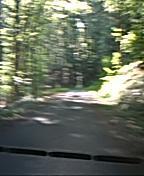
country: FR
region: Rhone-Alpes
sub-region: Departement de la Loire
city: La Pacaudiere
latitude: 46.1308
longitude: 3.7845
